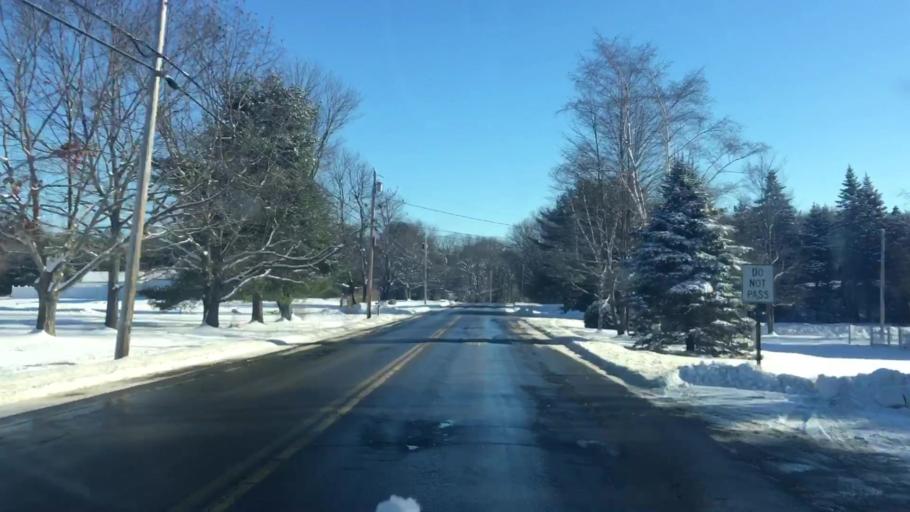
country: US
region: Maine
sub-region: Androscoggin County
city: Lisbon Falls
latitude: 43.9299
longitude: -70.0513
